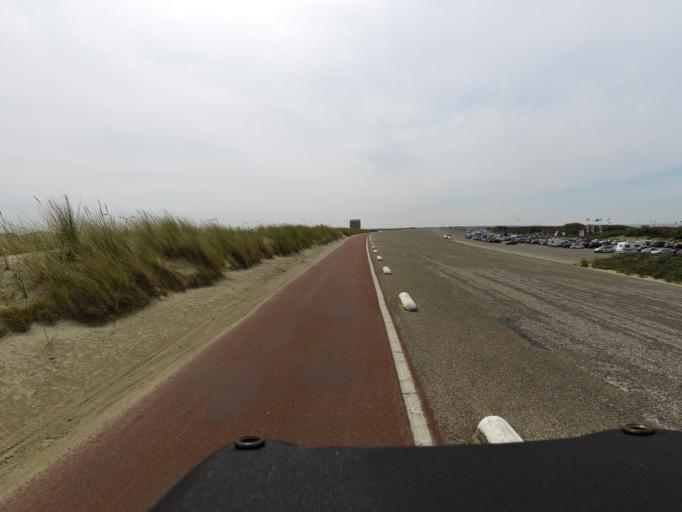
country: NL
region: Zeeland
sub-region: Schouwen-Duiveland
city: Scharendijke
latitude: 51.7629
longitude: 3.8549
